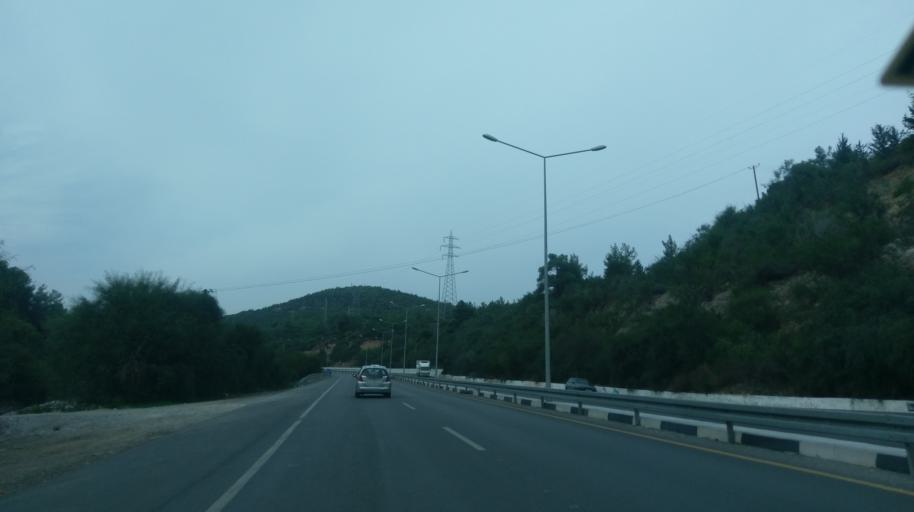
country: CY
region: Keryneia
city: Kyrenia
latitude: 35.3095
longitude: 33.3181
